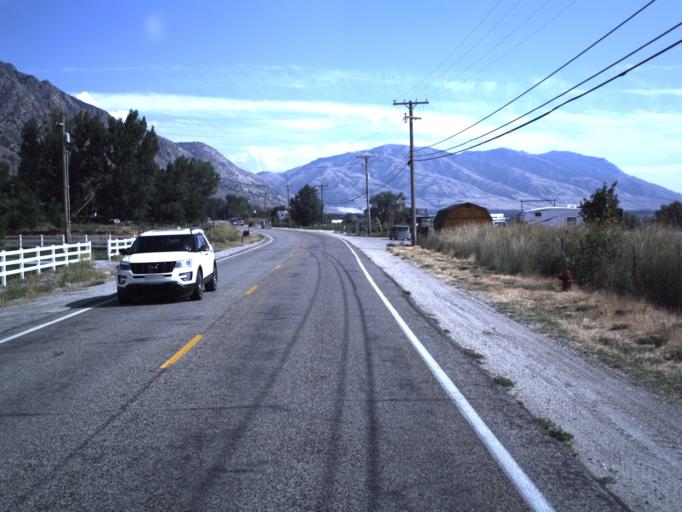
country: US
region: Utah
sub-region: Box Elder County
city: Honeyville
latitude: 41.5829
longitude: -112.0376
